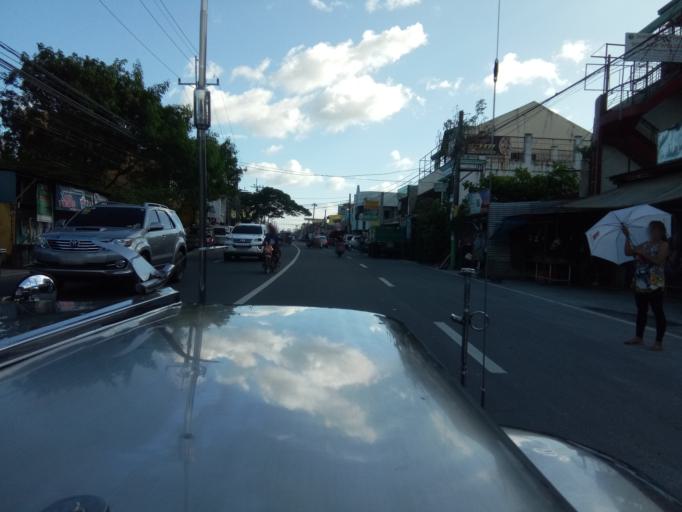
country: PH
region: Calabarzon
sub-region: Province of Cavite
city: Dasmarinas
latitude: 14.3499
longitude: 120.9809
